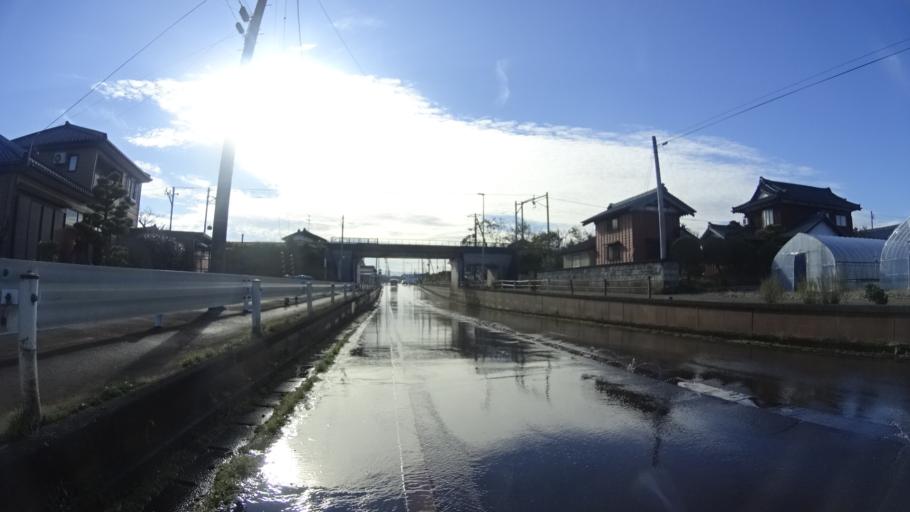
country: JP
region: Niigata
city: Yoshida-kasugacho
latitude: 37.6283
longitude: 138.8364
